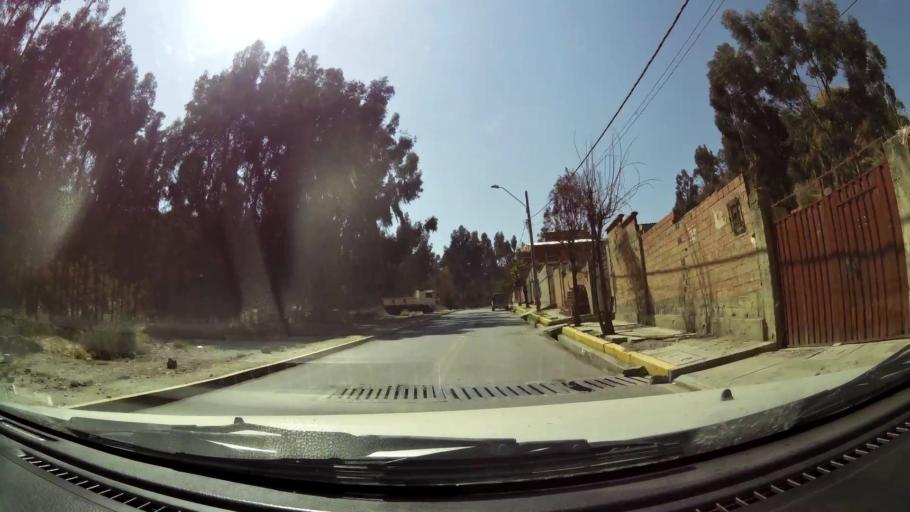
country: BO
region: La Paz
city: La Paz
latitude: -16.5374
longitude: -68.0438
